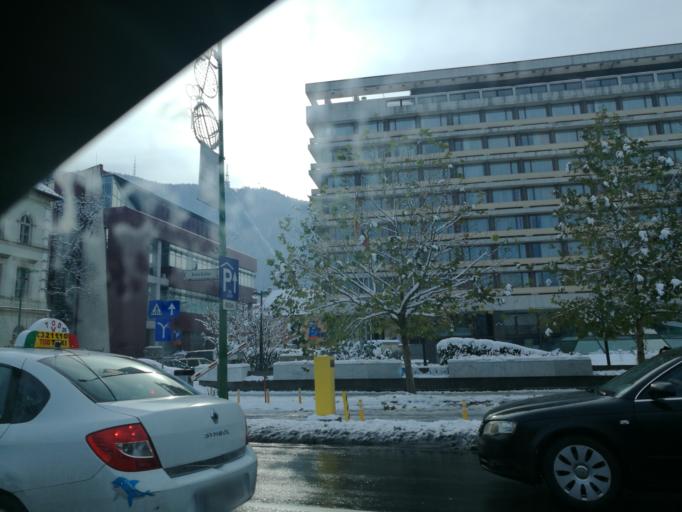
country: RO
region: Brasov
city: Brasov
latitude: 45.6452
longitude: 25.5917
